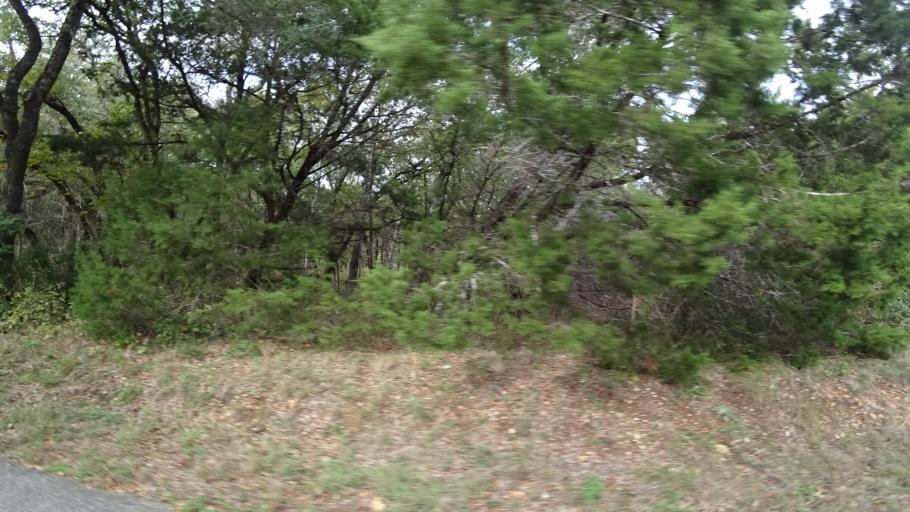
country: US
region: Texas
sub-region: Travis County
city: Shady Hollow
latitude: 30.1371
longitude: -97.8749
